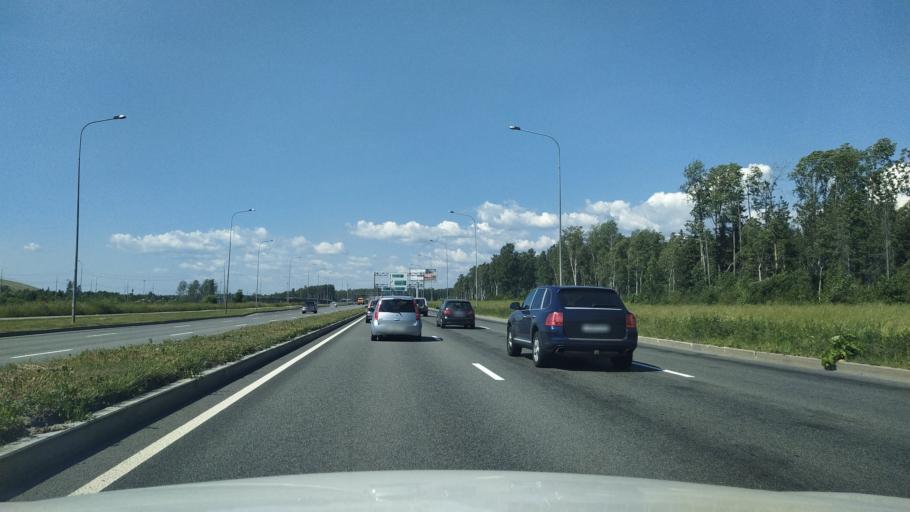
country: RU
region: St.-Petersburg
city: Levashovo
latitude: 60.0692
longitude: 30.1872
